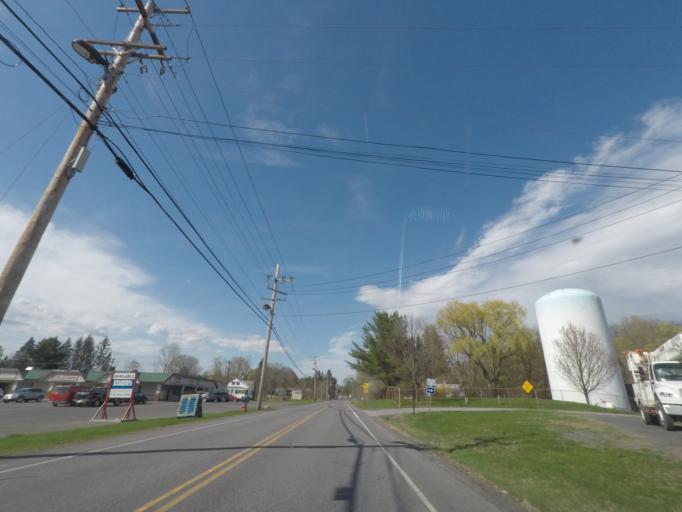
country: US
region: New York
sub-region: Greene County
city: Cairo
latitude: 42.4285
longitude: -74.0171
